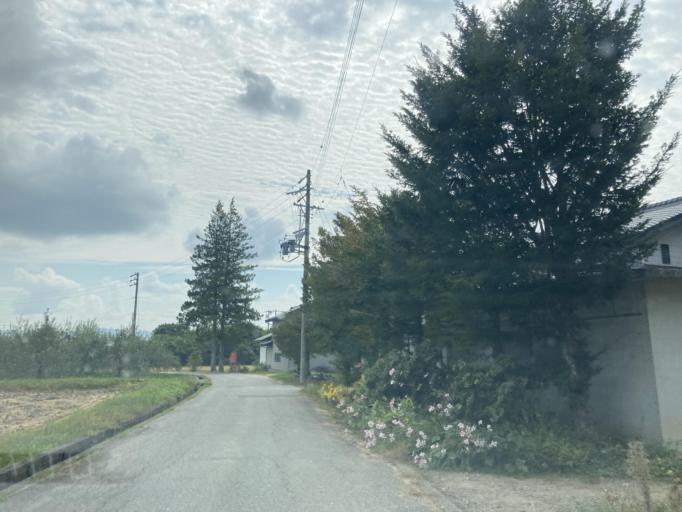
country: JP
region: Nagano
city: Omachi
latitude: 36.5288
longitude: 137.8204
